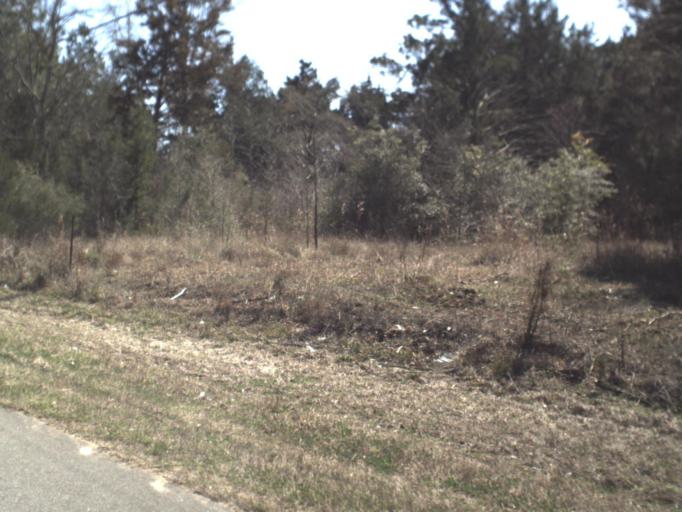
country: US
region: Florida
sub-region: Jackson County
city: Marianna
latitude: 30.7996
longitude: -85.2751
